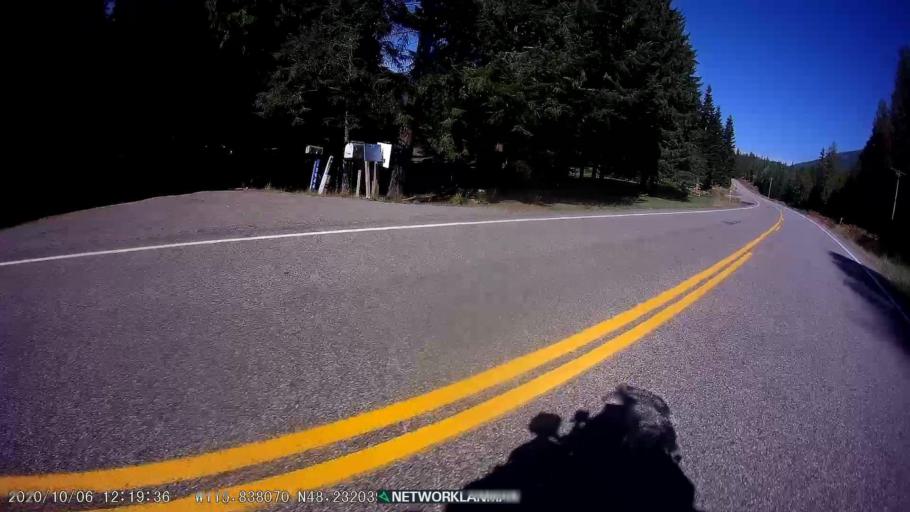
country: US
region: Montana
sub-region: Lincoln County
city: Libby
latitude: 48.2322
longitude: -115.8380
